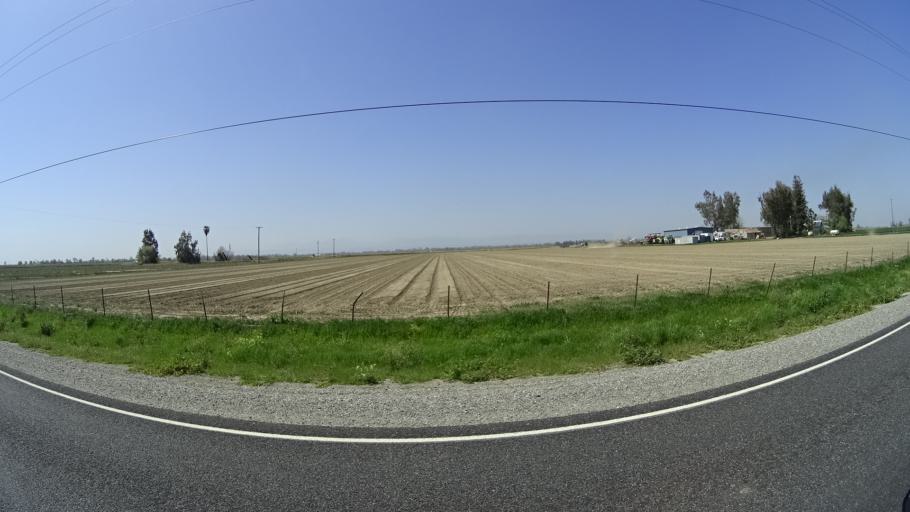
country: US
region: California
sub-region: Glenn County
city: Willows
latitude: 39.5317
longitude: -122.1365
